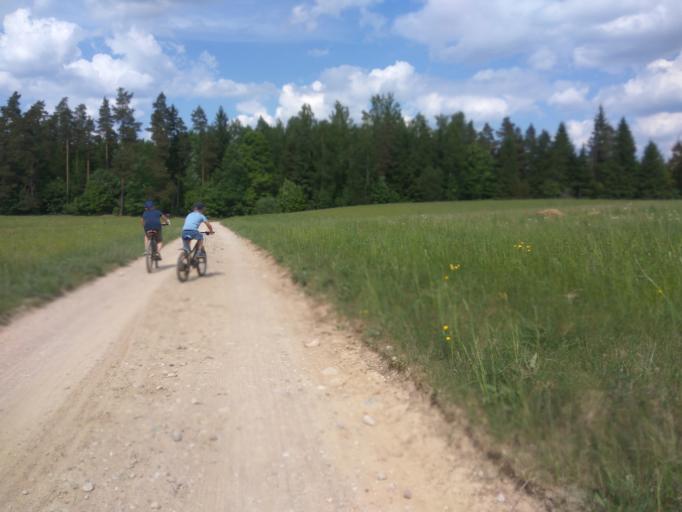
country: LV
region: Kuldigas Rajons
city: Kuldiga
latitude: 56.9023
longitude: 21.9247
